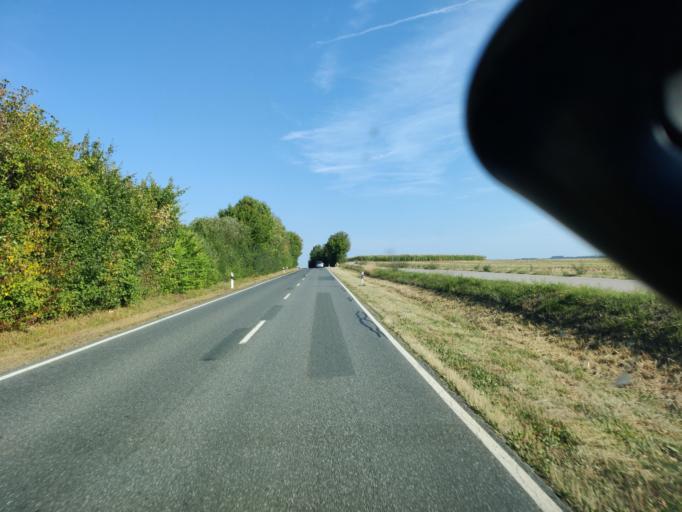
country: DE
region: Bavaria
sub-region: Regierungsbezirk Mittelfranken
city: Hilpoltstein
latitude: 49.1772
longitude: 11.2261
